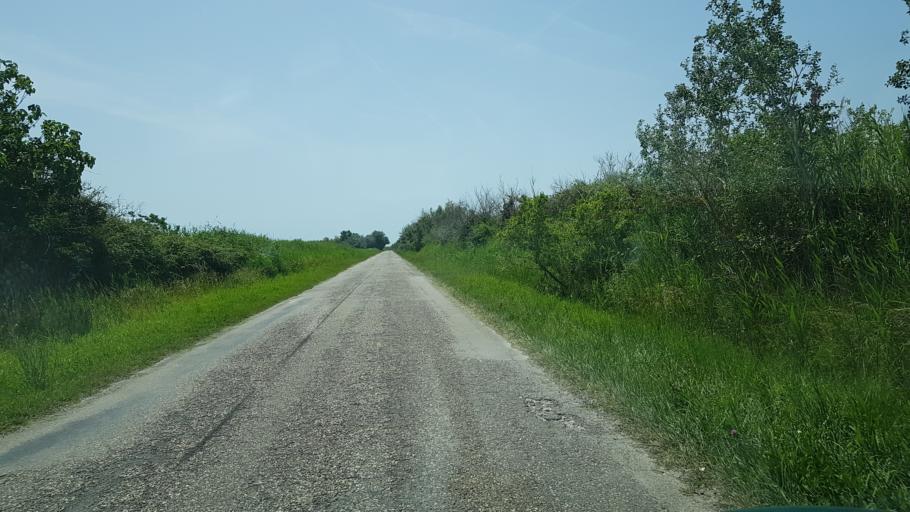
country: FR
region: Provence-Alpes-Cote d'Azur
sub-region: Departement des Bouches-du-Rhone
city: Arles
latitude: 43.5593
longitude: 4.6241
